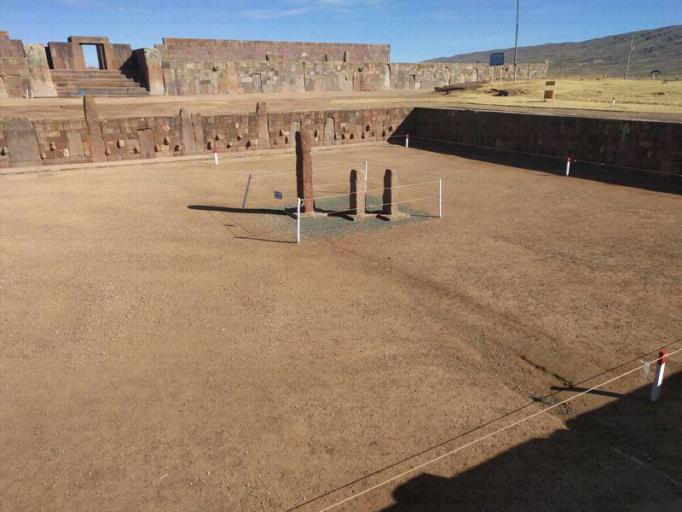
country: BO
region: La Paz
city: Tiahuanaco
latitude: -16.5548
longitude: -68.6723
